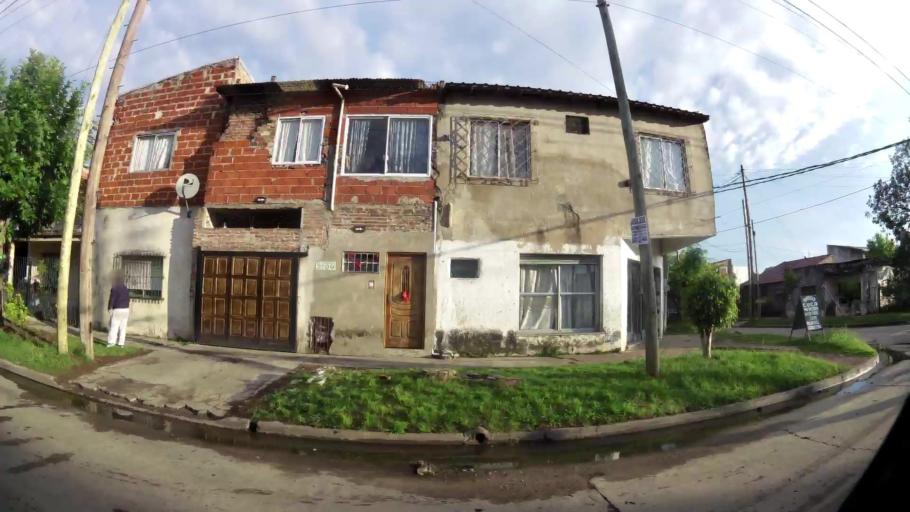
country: AR
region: Buenos Aires
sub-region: Partido de Lomas de Zamora
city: Lomas de Zamora
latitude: -34.7562
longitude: -58.3545
